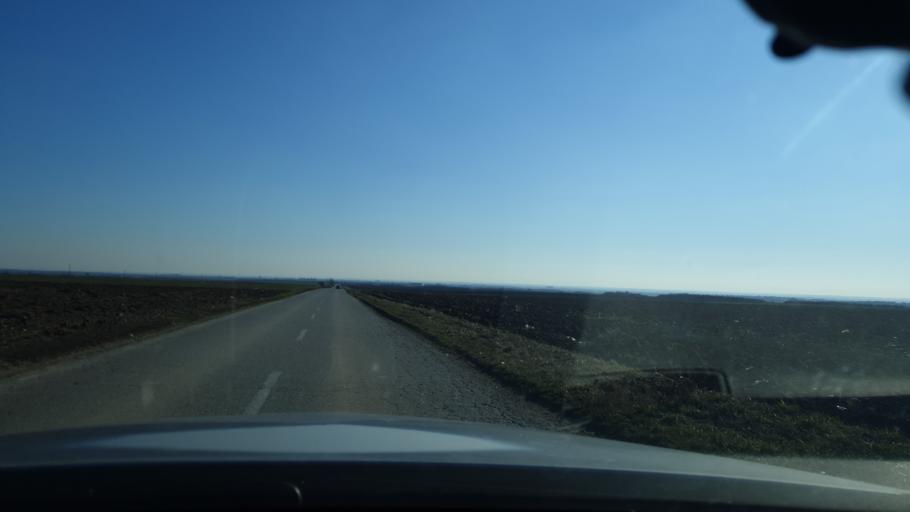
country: RS
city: Vrdnik
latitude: 45.0864
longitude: 19.8068
